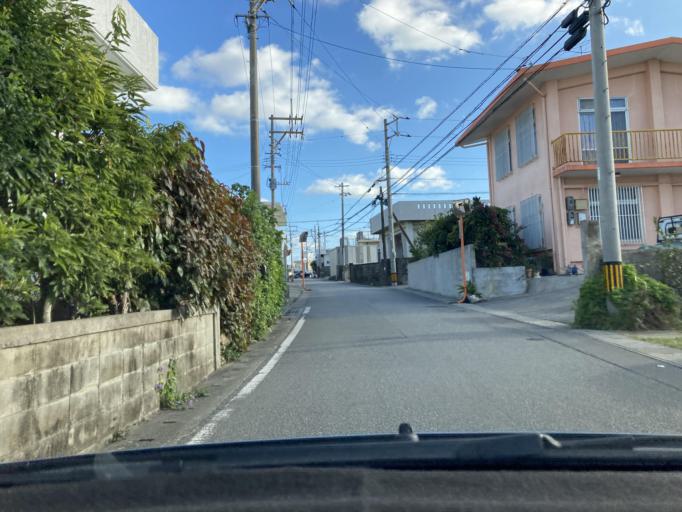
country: JP
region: Okinawa
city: Gushikawa
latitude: 26.3612
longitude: 127.8554
